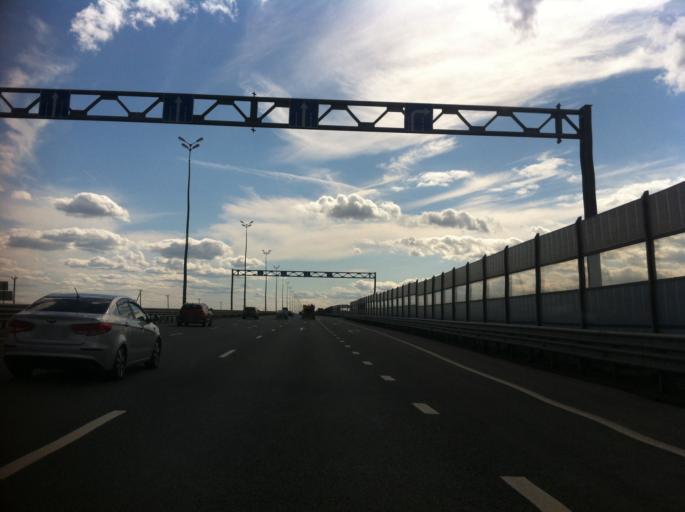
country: RU
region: Leningrad
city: Maloye Verevo
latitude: 59.6436
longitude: 30.2221
